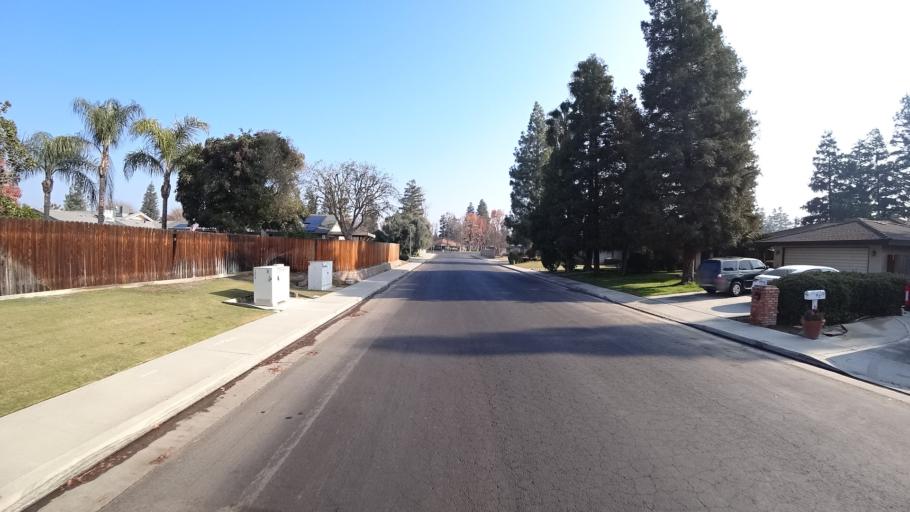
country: US
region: California
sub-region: Kern County
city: Greenacres
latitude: 35.3303
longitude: -119.0865
